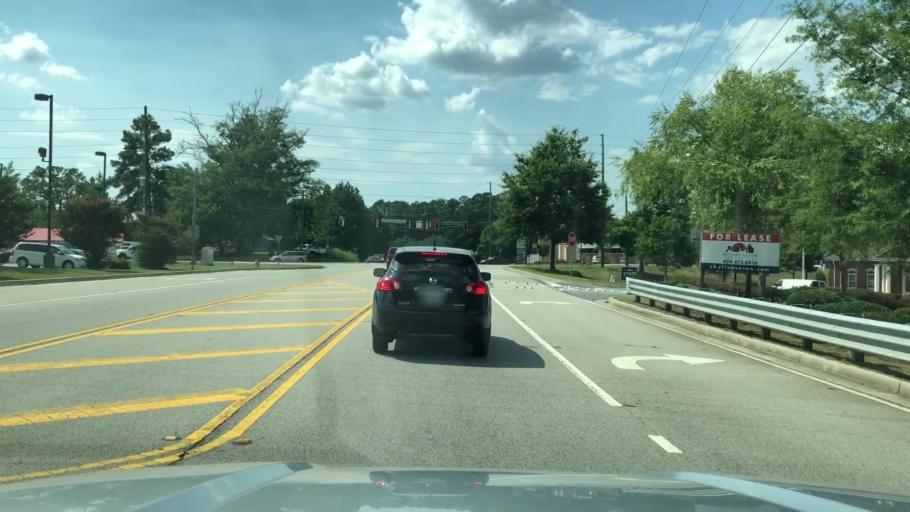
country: US
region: Georgia
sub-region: Paulding County
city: Dallas
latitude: 33.9579
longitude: -84.7883
